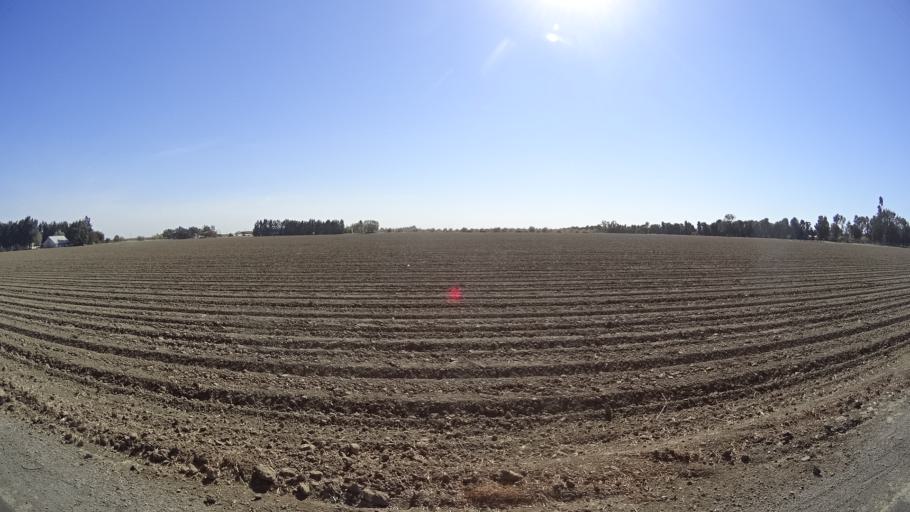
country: US
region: California
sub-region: Yolo County
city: Woodland
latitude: 38.6415
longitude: -121.7894
